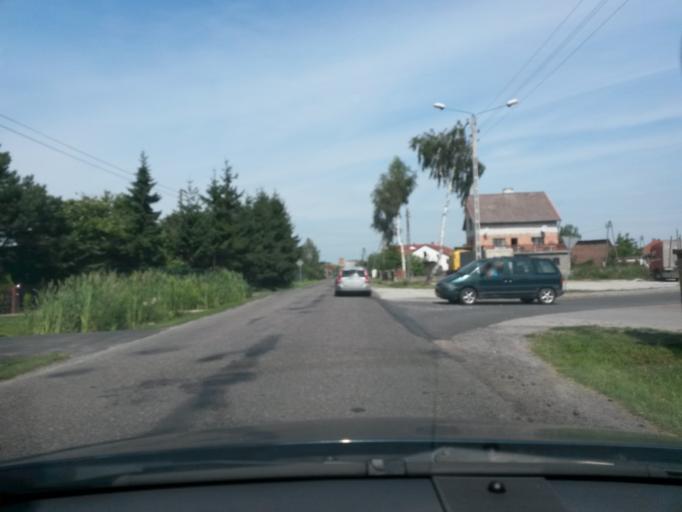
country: PL
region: Lower Silesian Voivodeship
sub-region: Powiat legnicki
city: Prochowice
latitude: 51.2676
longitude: 16.3657
